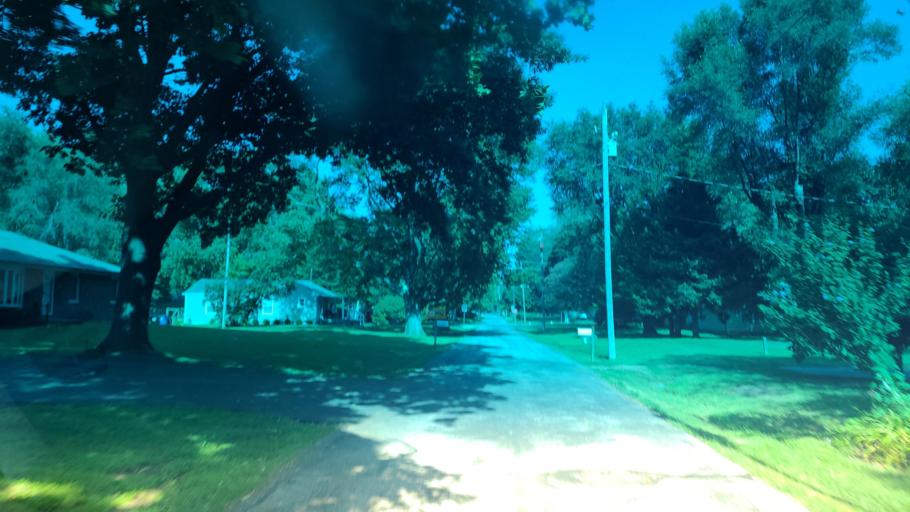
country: US
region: Kansas
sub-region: Douglas County
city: Lawrence
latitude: 38.9842
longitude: -95.2254
